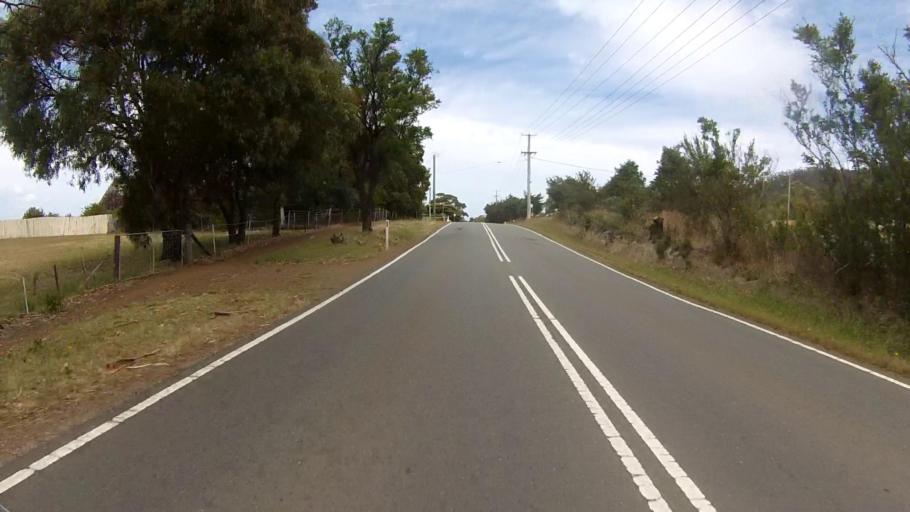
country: AU
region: Tasmania
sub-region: Clarence
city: Acton Park
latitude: -42.8910
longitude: 147.4823
